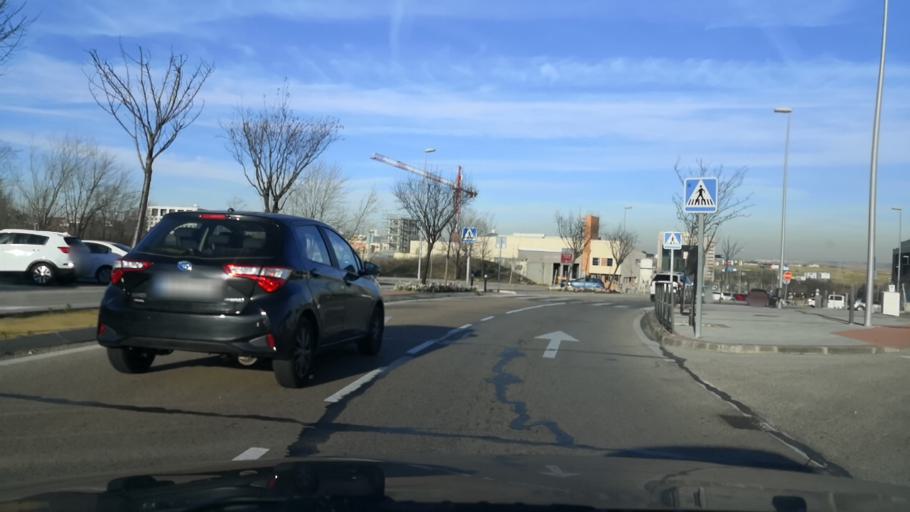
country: ES
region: Madrid
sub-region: Provincia de Madrid
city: San Sebastian de los Reyes
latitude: 40.5342
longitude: -3.6193
